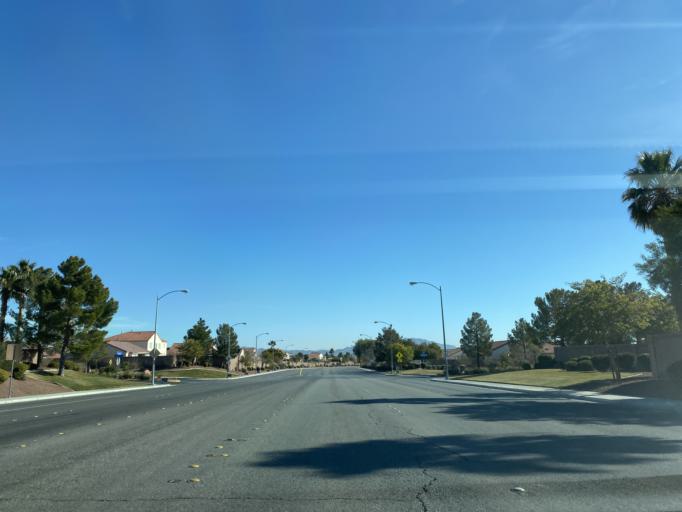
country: US
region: Nevada
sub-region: Clark County
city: North Las Vegas
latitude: 36.2825
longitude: -115.1480
